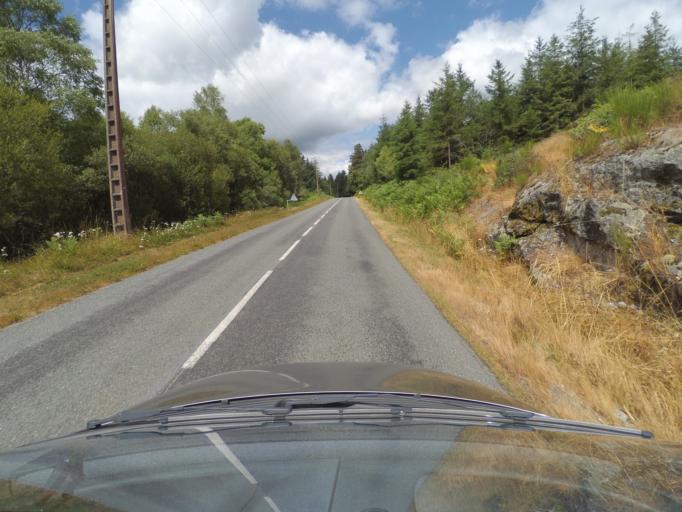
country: FR
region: Limousin
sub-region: Departement de la Haute-Vienne
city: Peyrat-le-Chateau
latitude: 45.8768
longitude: 1.8976
